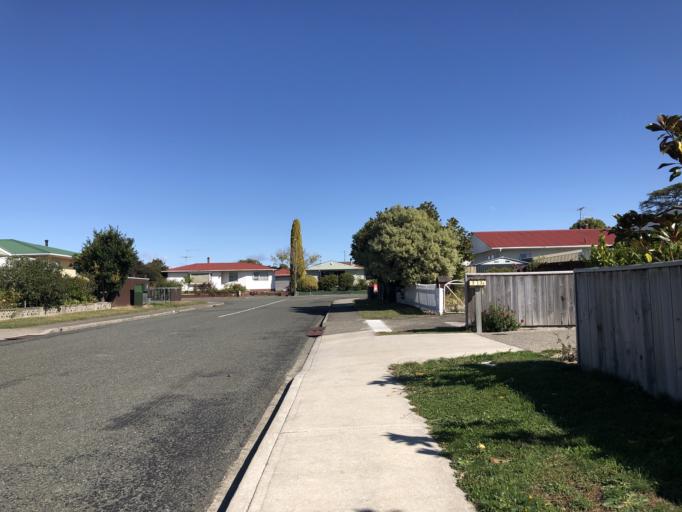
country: NZ
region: Tasman
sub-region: Tasman District
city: Richmond
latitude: -41.3433
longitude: 173.1749
